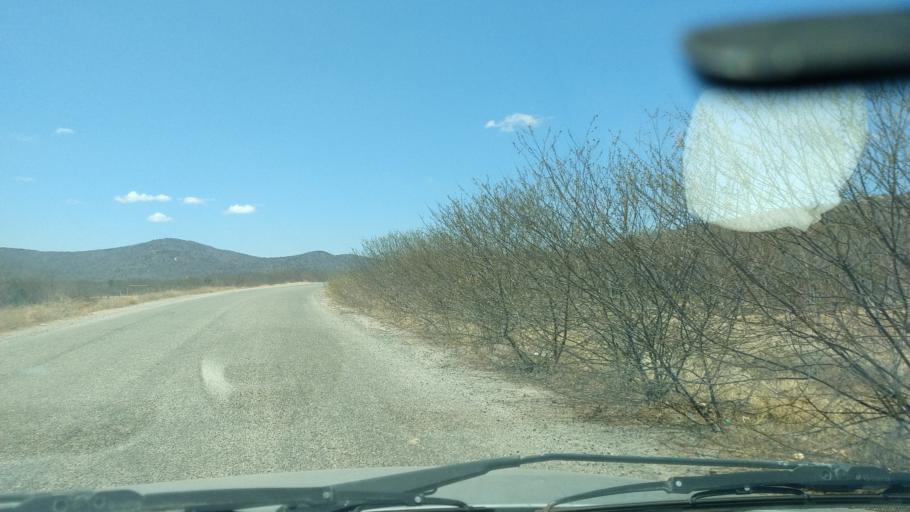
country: BR
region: Rio Grande do Norte
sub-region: Sao Tome
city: Sao Tome
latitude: -5.9726
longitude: -36.1357
